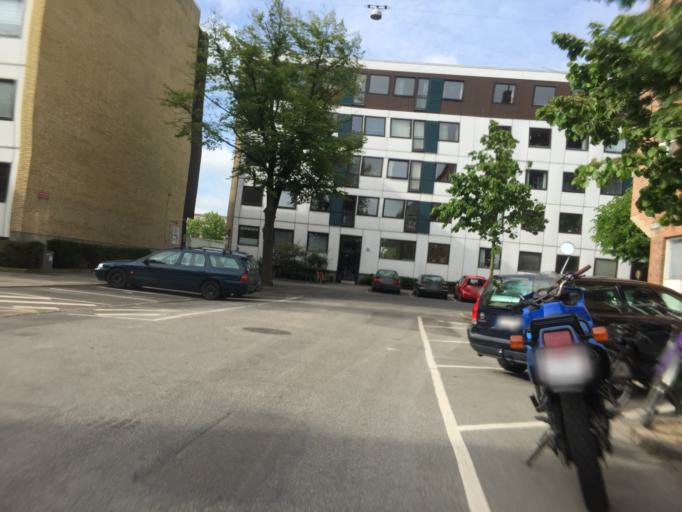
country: DK
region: Capital Region
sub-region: Frederiksberg Kommune
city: Frederiksberg
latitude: 55.6826
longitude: 12.5269
